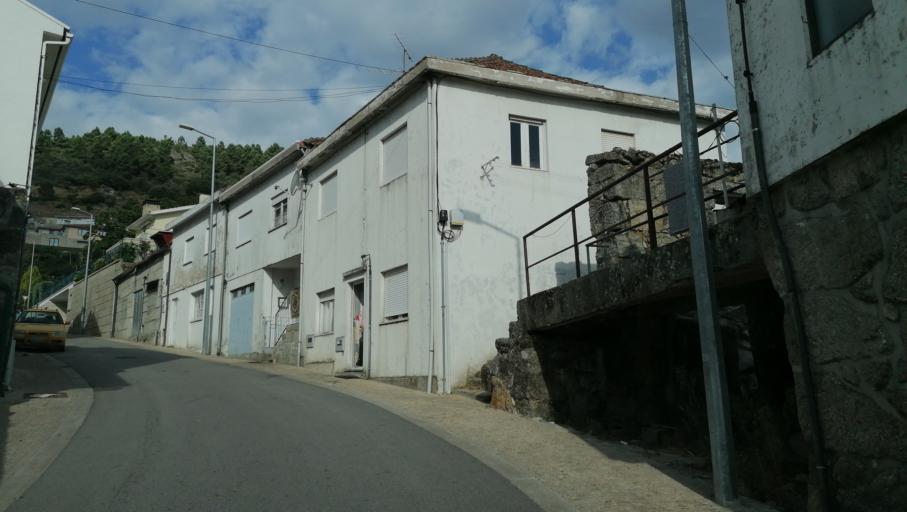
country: PT
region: Vila Real
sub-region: Vila Pouca de Aguiar
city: Vila Pouca de Aguiar
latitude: 41.5023
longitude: -7.6478
